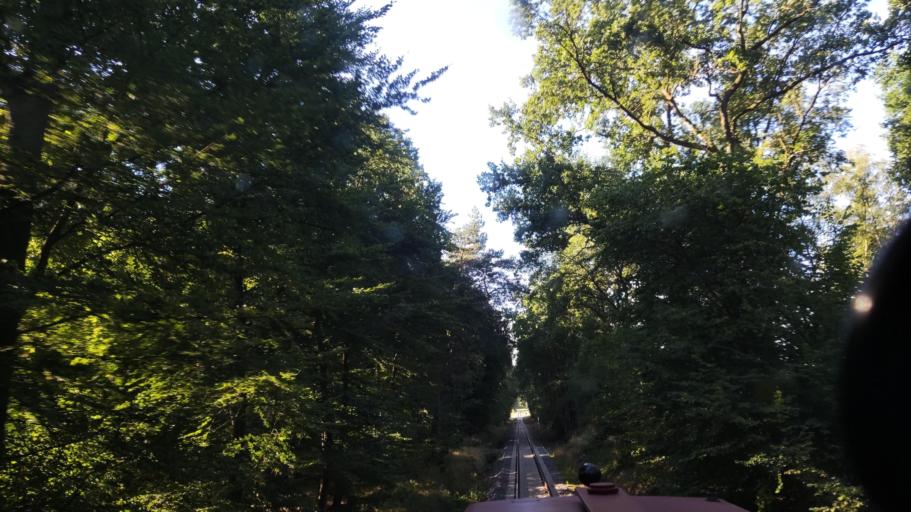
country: DE
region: Lower Saxony
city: Melbeck
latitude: 53.2039
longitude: 10.3798
